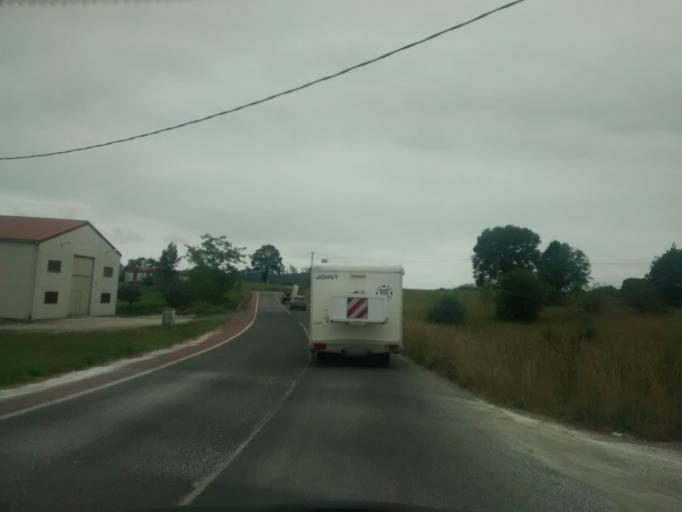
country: ES
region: Cantabria
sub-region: Provincia de Cantabria
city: Luzmela
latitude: 43.3093
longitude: -4.1968
